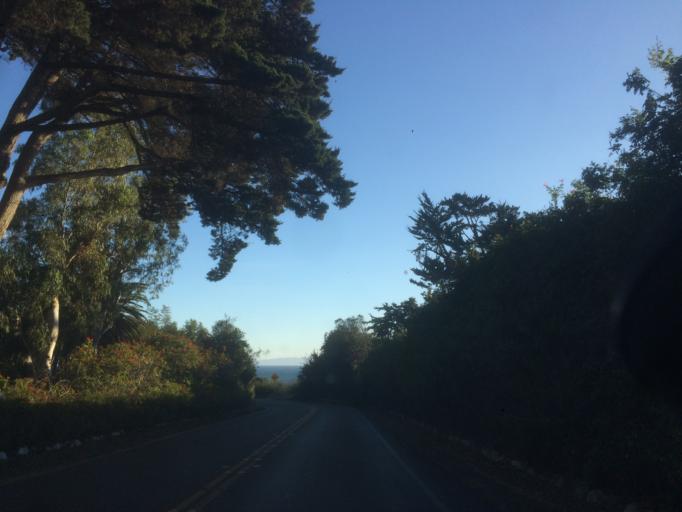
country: US
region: California
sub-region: Santa Barbara County
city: Santa Barbara
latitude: 34.4086
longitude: -119.7562
